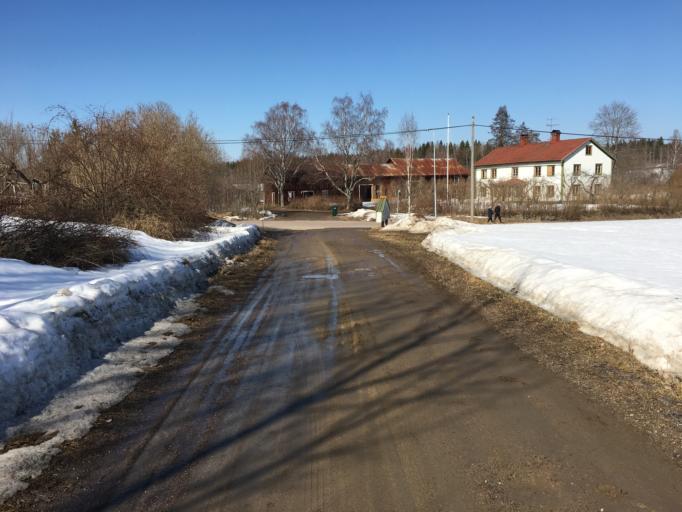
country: SE
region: Gaevleborg
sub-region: Hofors Kommun
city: Hofors
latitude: 60.5150
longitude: 16.4389
